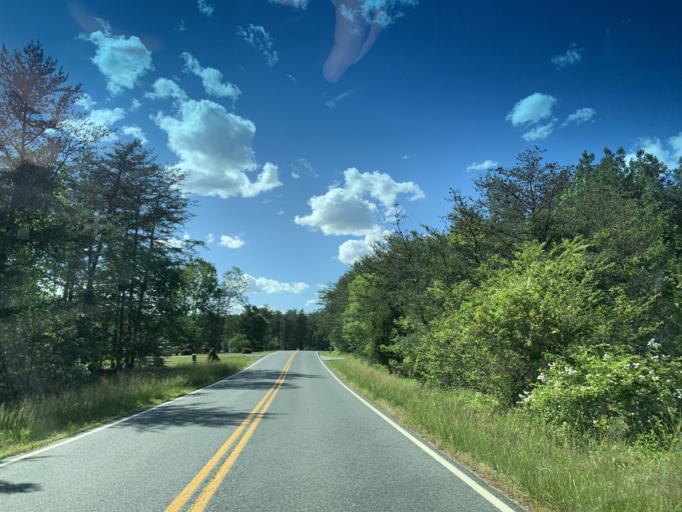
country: US
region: Maryland
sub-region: Cecil County
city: North East
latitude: 39.5573
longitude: -75.9254
